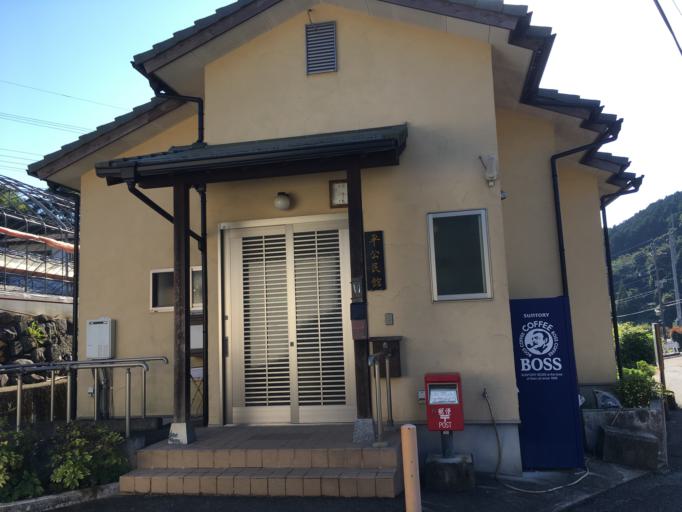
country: JP
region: Kumamoto
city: Kumamoto
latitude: 32.7982
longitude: 130.6581
